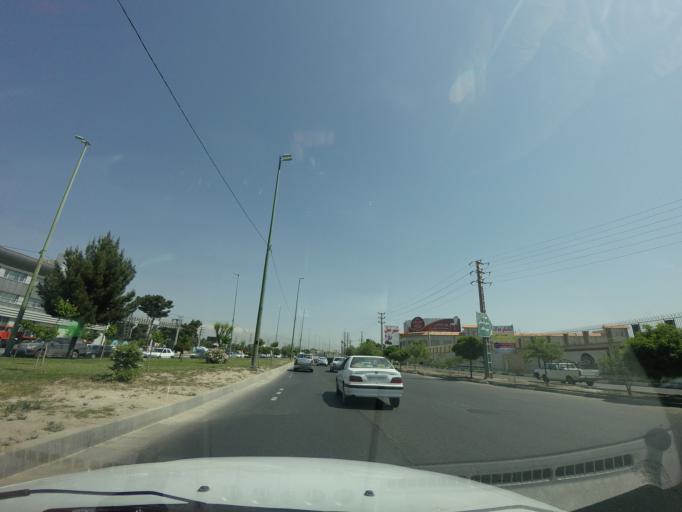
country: IR
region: Tehran
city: Eslamshahr
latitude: 35.5956
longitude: 51.2955
